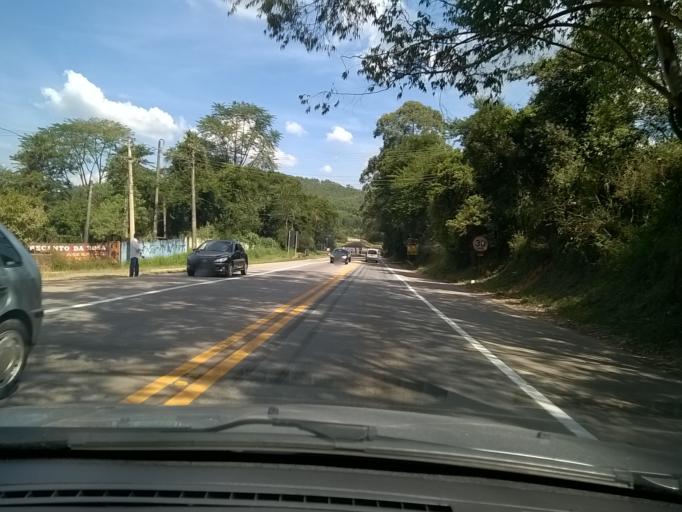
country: BR
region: Sao Paulo
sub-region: Varzea Paulista
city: Varzea Paulista
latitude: -23.2561
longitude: -46.8360
